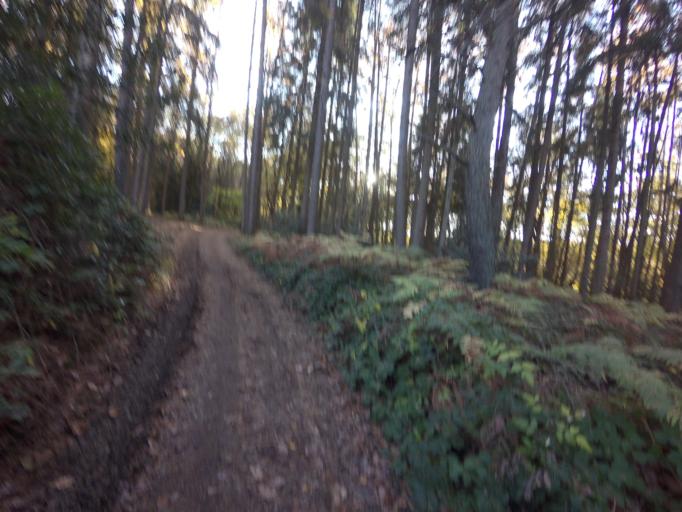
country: BE
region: Wallonia
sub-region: Province de Liege
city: Plombieres
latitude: 50.7740
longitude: 5.9677
